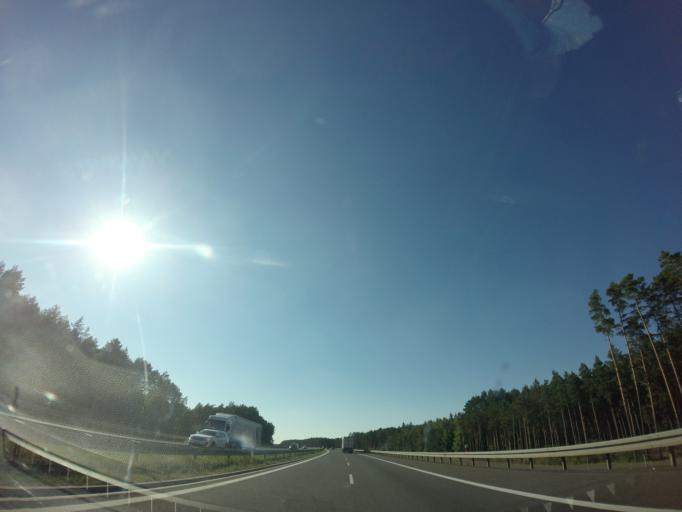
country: PL
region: Lubusz
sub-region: Powiat gorzowski
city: Deszczno
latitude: 52.6384
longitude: 15.3673
